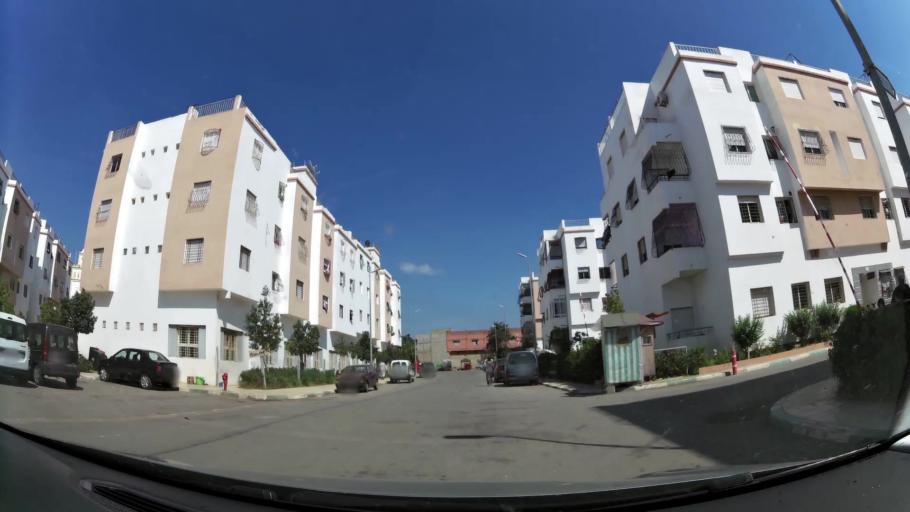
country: MA
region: Rabat-Sale-Zemmour-Zaer
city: Sale
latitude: 34.0696
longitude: -6.7556
